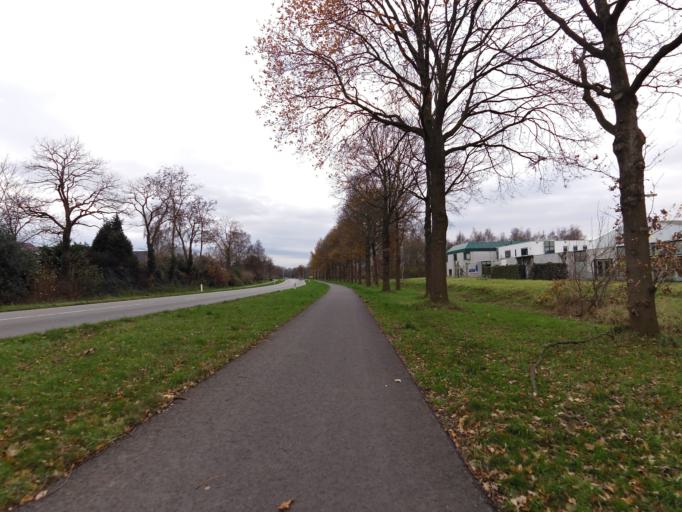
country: NL
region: Gelderland
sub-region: Gemeente Zevenaar
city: Zevenaar
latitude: 51.9437
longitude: 6.1212
